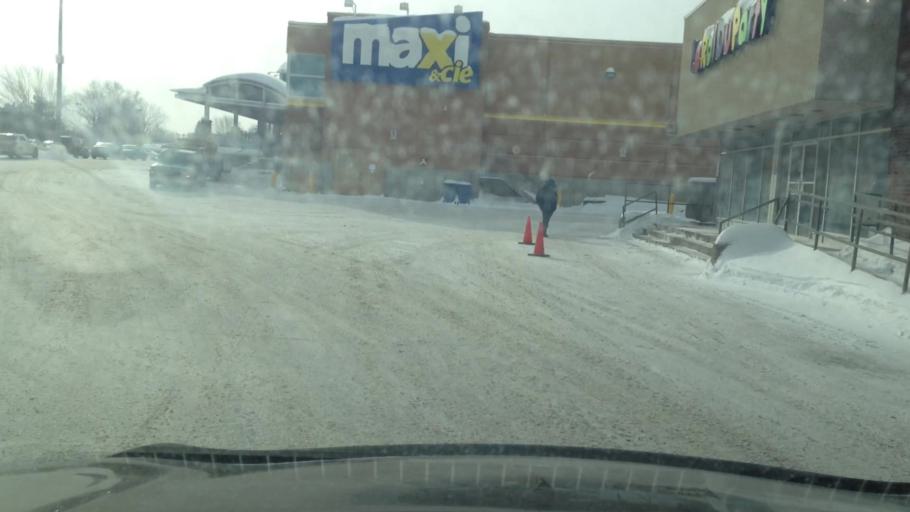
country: CA
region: Quebec
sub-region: Laurentides
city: Saint-Jerome
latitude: 45.7939
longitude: -74.0171
